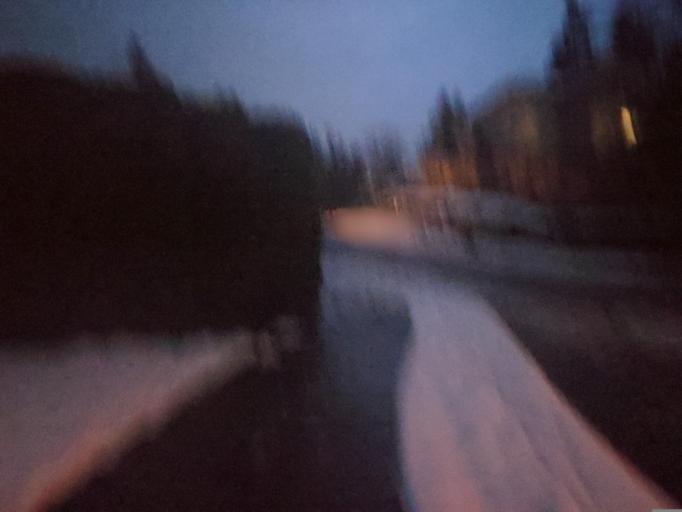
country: US
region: Washington
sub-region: King County
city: West Lake Sammamish
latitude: 47.5538
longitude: -122.1205
